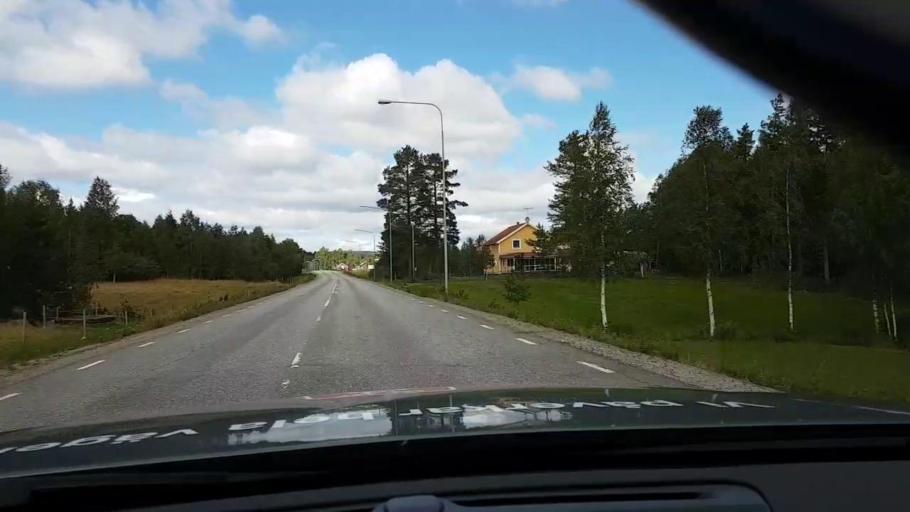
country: SE
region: Vaesternorrland
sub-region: OErnskoeldsviks Kommun
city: Bredbyn
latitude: 63.4771
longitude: 18.0942
